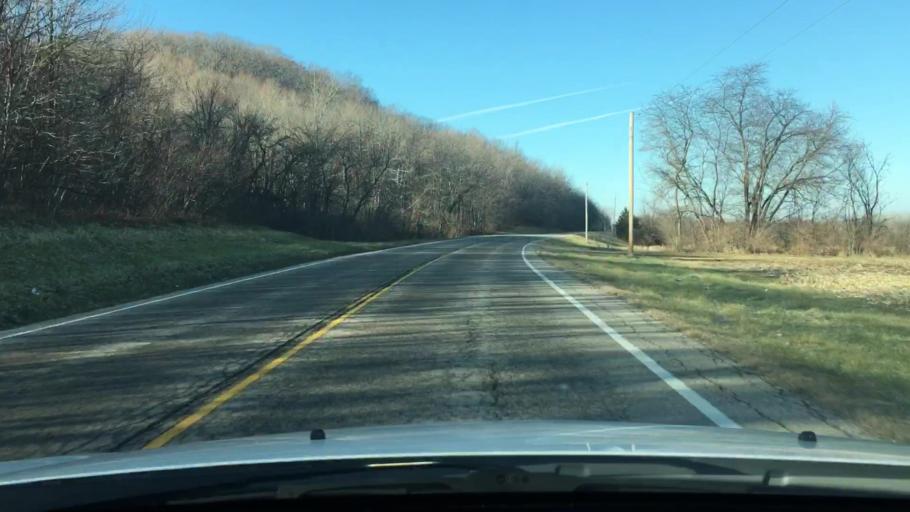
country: US
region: Illinois
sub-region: Bureau County
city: Spring Valley
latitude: 41.3006
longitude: -89.1782
